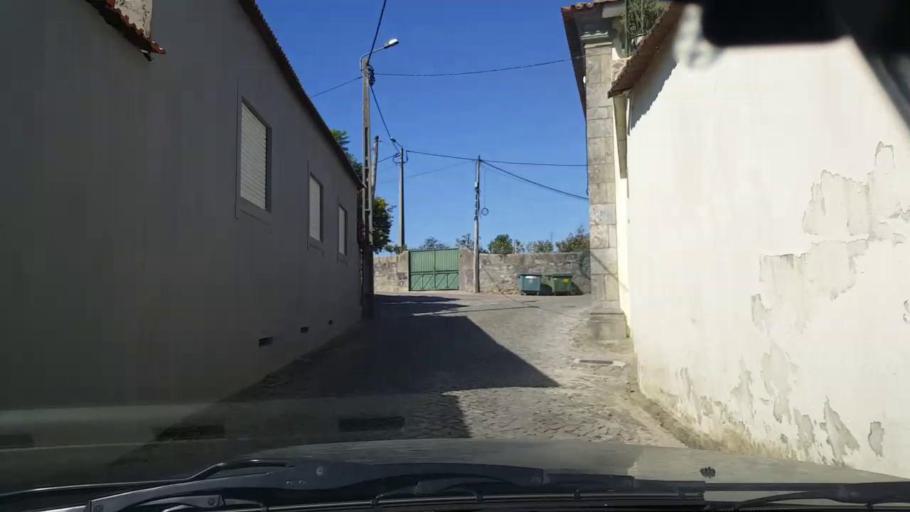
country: PT
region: Porto
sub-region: Vila do Conde
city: Arvore
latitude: 41.3120
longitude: -8.6733
